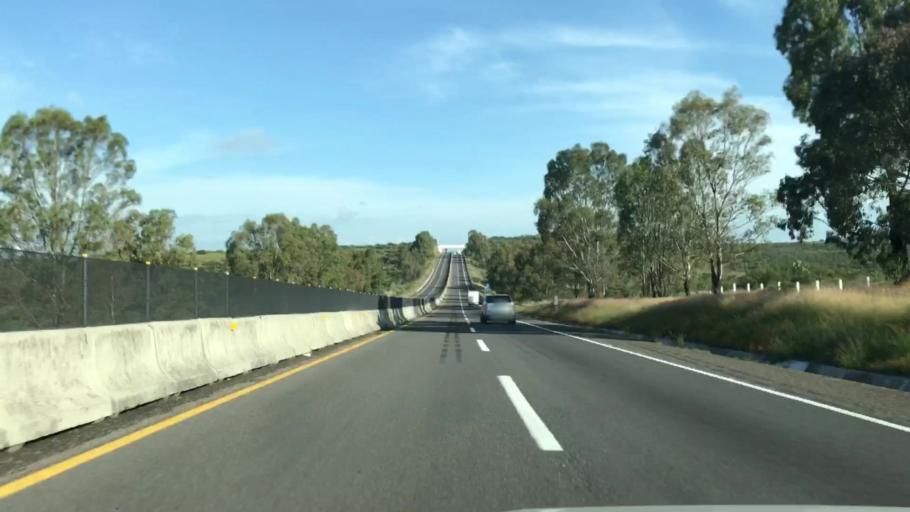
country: MX
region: Jalisco
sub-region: Lagos de Moreno
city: Cristeros [Fraccionamiento]
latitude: 21.3768
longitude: -102.1364
